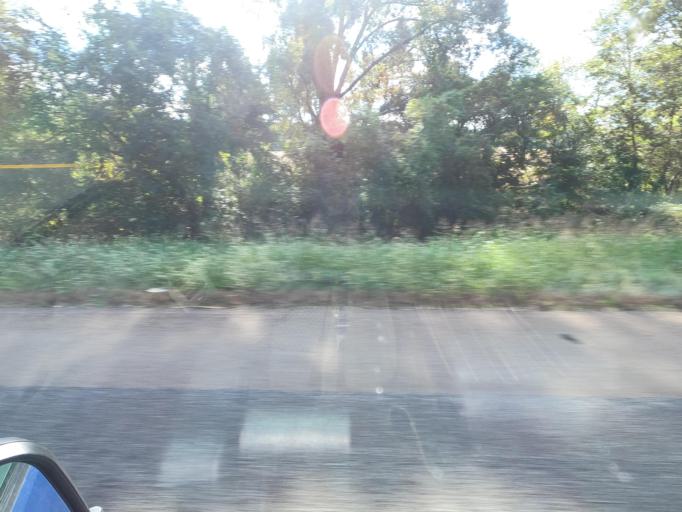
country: US
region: Tennessee
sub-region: Haywood County
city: Brownsville
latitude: 35.5437
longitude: -89.2236
